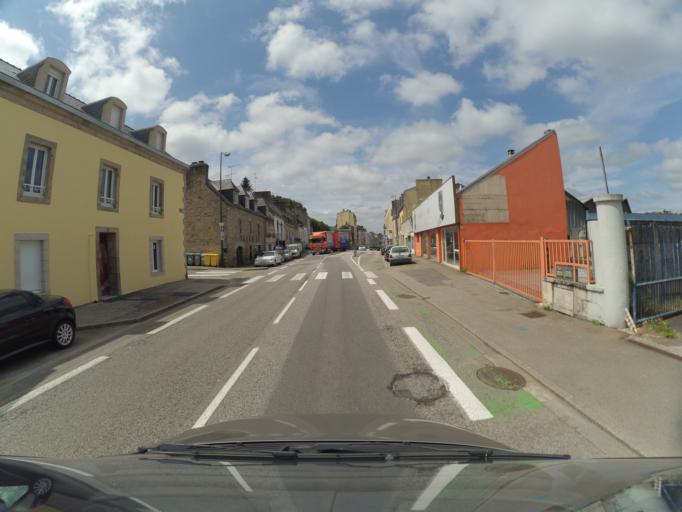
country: FR
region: Brittany
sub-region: Departement du Finistere
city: Quimper
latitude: 47.9925
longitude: -4.0811
